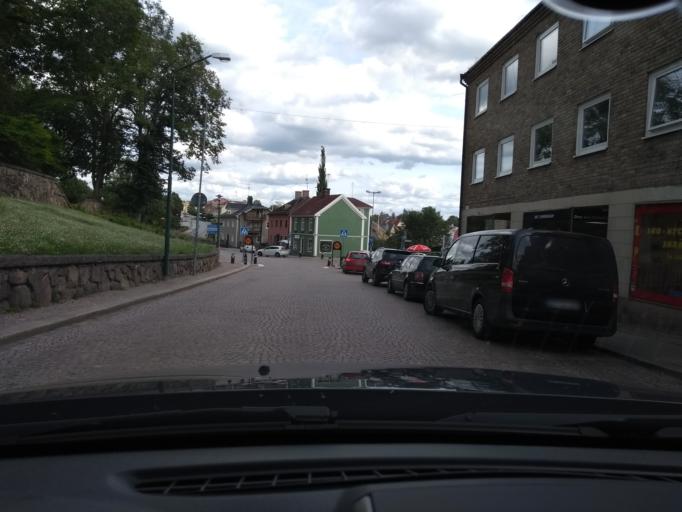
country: SE
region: Kalmar
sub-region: Vimmerby Kommun
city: Vimmerby
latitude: 57.6652
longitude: 15.8573
